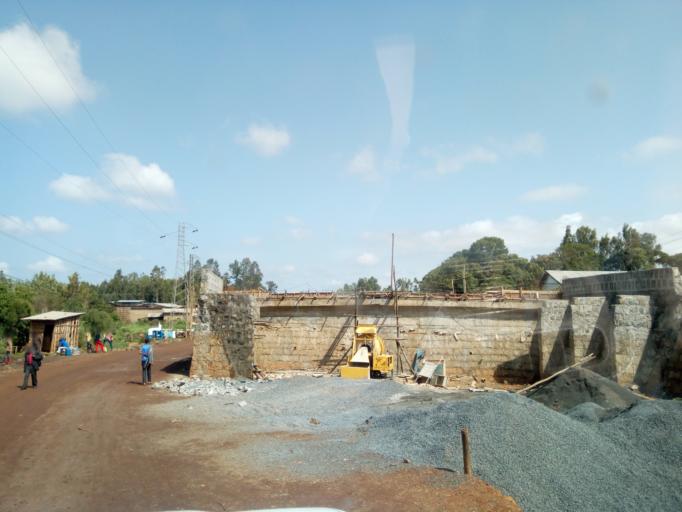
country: ET
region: Oromiya
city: Waliso
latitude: 8.5444
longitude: 37.9680
